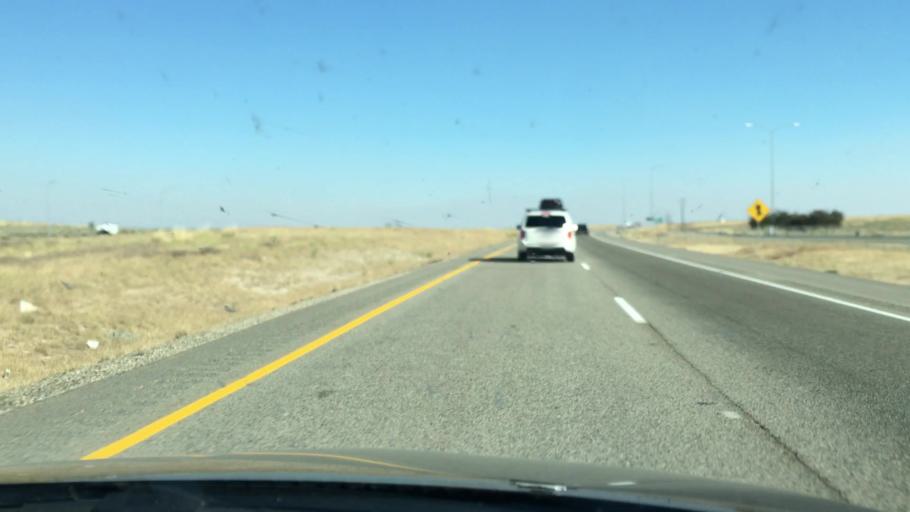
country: US
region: Idaho
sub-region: Ada County
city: Boise
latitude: 43.4778
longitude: -116.1070
